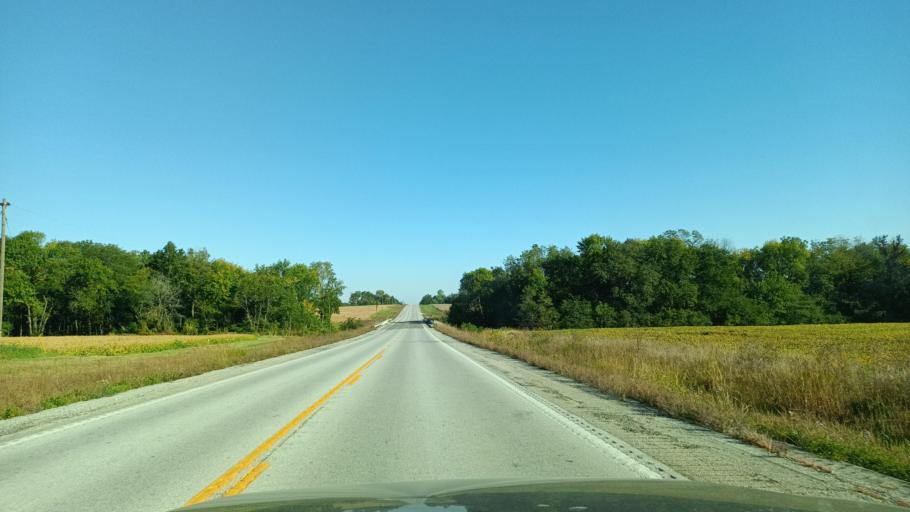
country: US
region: Missouri
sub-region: Audrain County
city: Vandalia
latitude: 39.3355
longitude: -91.6430
